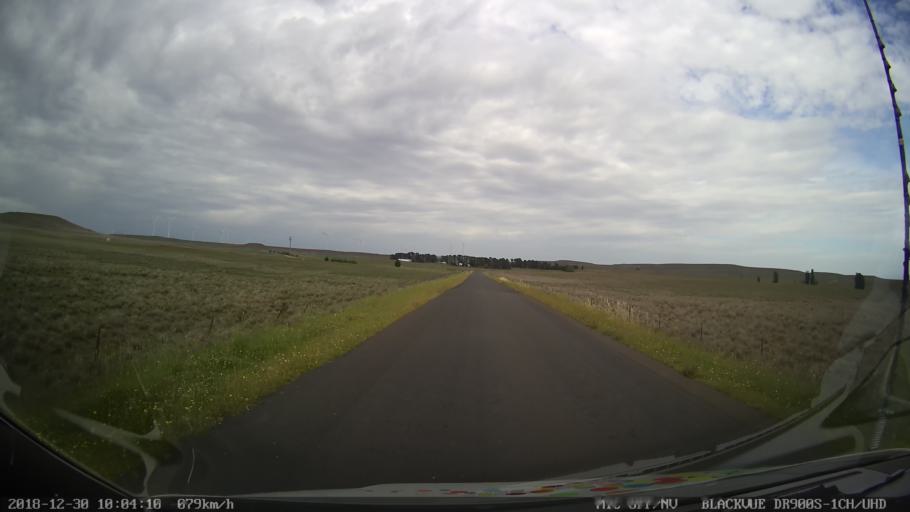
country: AU
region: New South Wales
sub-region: Cooma-Monaro
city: Cooma
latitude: -36.5197
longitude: 149.1489
